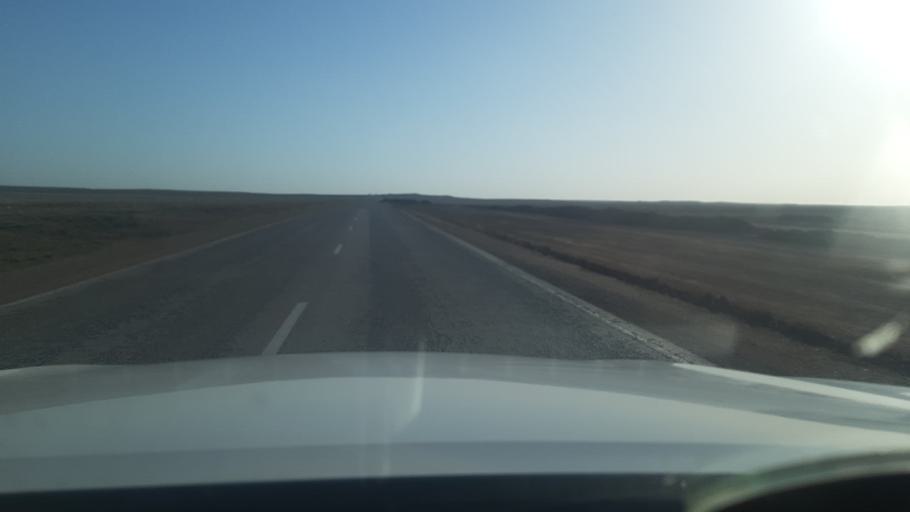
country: KZ
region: Qaraghandy
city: Saryshaghan
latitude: 46.4121
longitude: 73.9039
